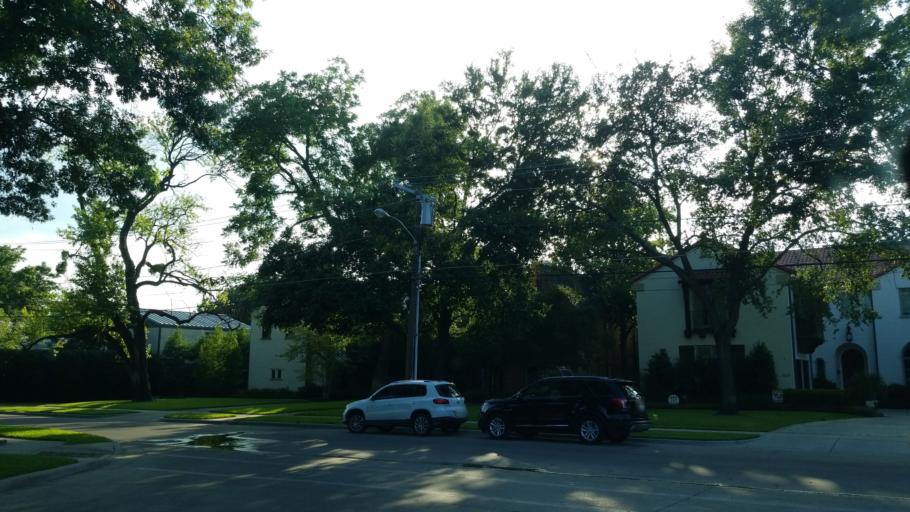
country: US
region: Texas
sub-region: Dallas County
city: University Park
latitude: 32.8473
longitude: -96.7947
